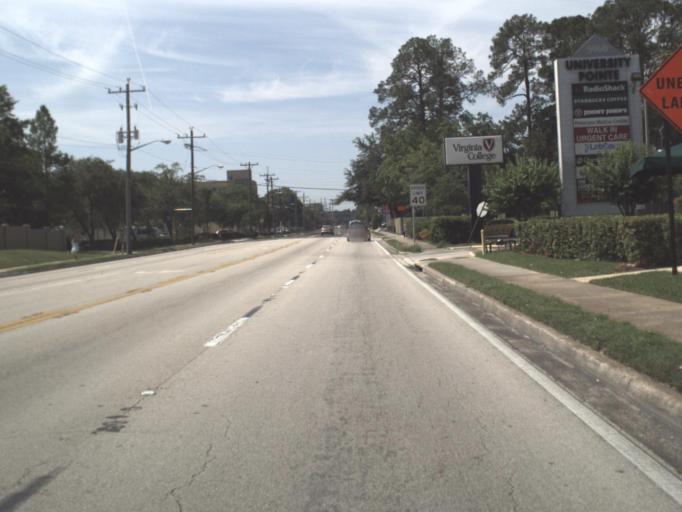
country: US
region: Florida
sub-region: Duval County
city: Jacksonville
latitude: 30.2920
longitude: -81.6021
